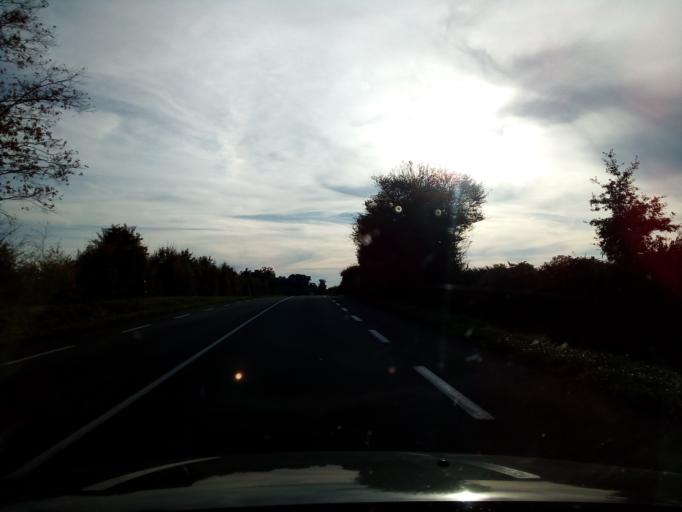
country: FR
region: Poitou-Charentes
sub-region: Departement de la Charente
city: Saint-Claud
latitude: 45.9117
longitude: 0.4927
